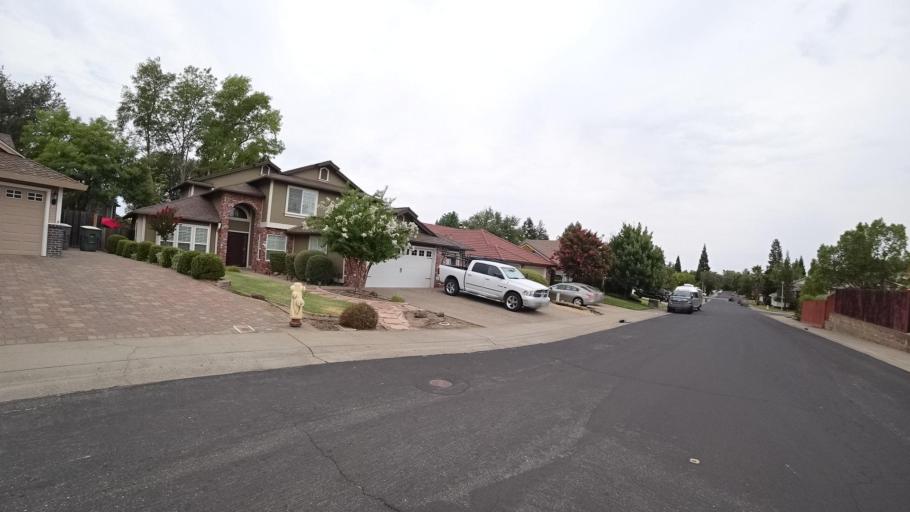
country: US
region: California
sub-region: Placer County
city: Rocklin
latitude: 38.7818
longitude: -121.2100
